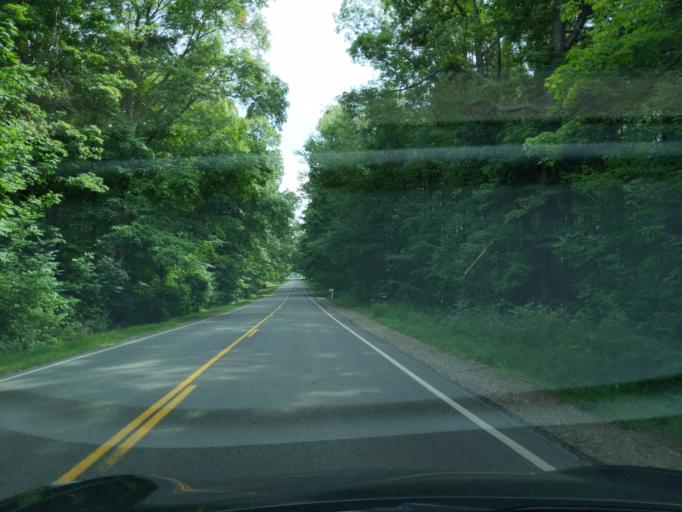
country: US
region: Michigan
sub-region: Eaton County
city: Dimondale
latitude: 42.6347
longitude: -84.6029
